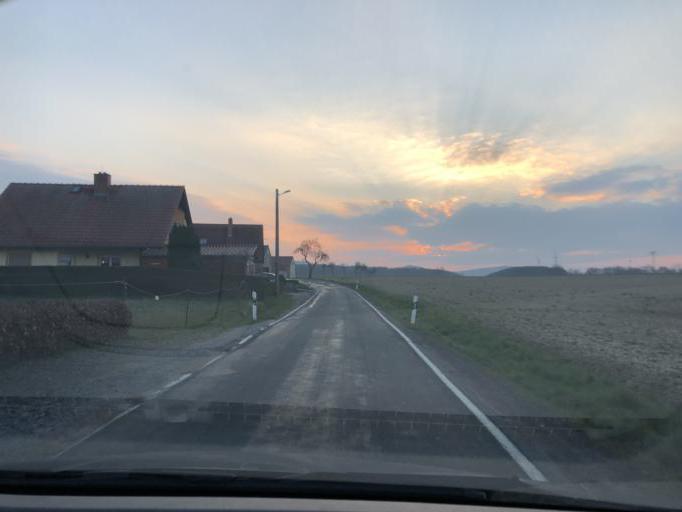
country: DE
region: Saxony
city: Panschwitz-Kuckau
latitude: 51.2313
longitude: 14.1822
